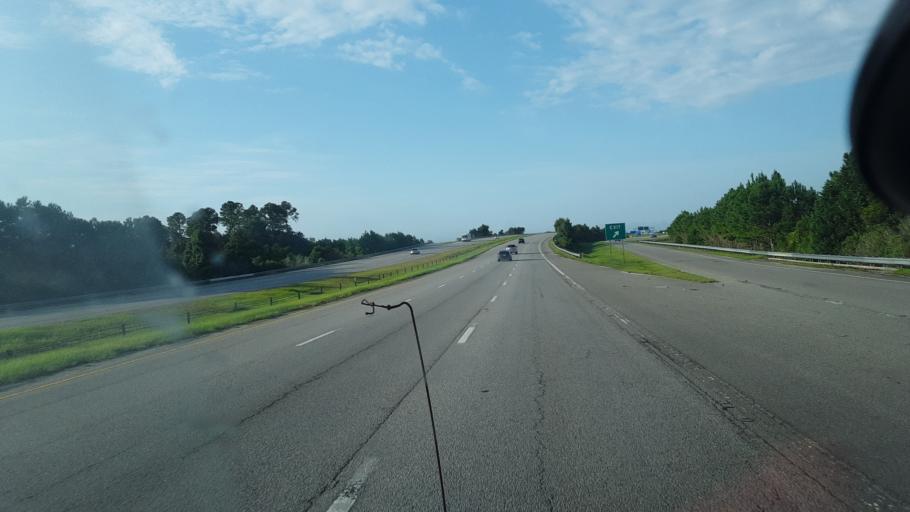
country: US
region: South Carolina
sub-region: Horry County
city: North Myrtle Beach
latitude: 33.8498
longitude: -78.6992
